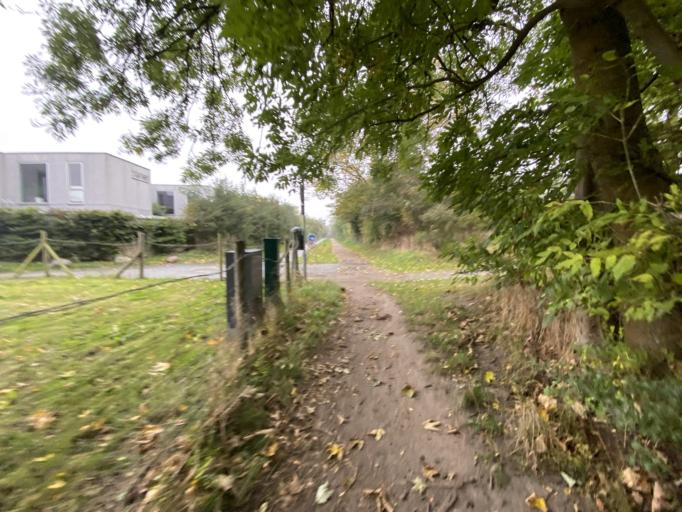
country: DK
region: Capital Region
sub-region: Dragor Kommune
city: Dragor
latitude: 55.5981
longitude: 12.6545
